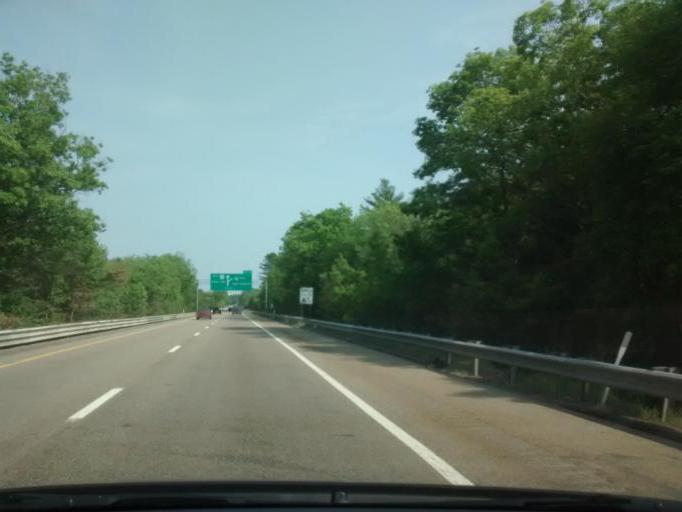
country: US
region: Massachusetts
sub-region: Plymouth County
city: West Wareham
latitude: 41.8042
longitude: -70.7666
